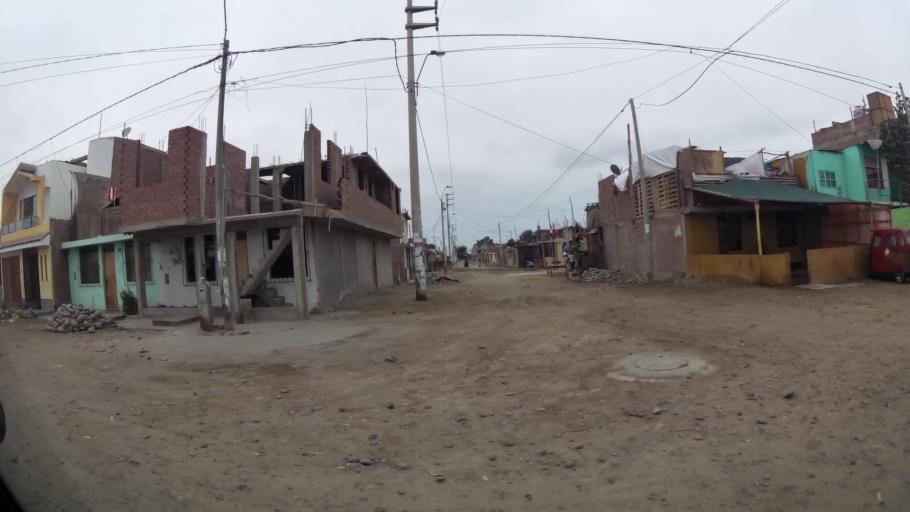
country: PE
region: Ica
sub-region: Provincia de Pisco
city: Pisco
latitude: -13.7308
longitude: -76.2007
